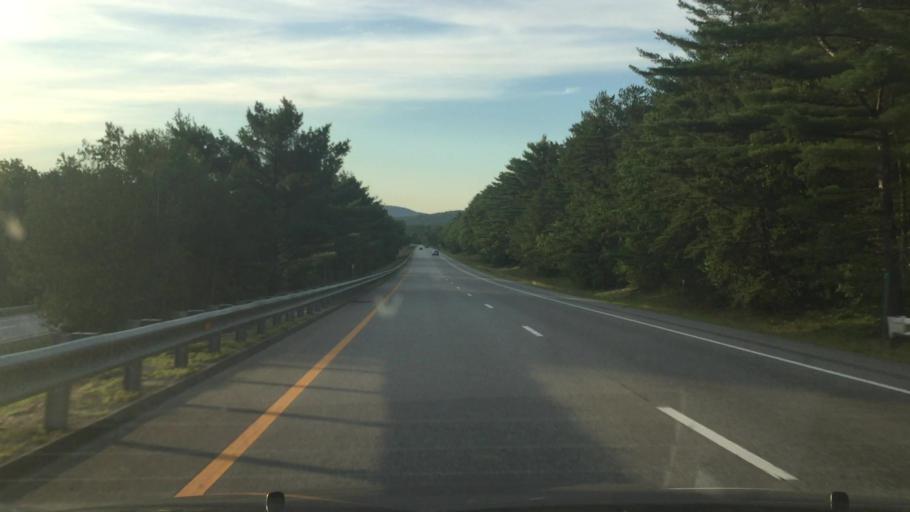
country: US
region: New Hampshire
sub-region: Grafton County
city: Plymouth
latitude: 43.7301
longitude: -71.6573
